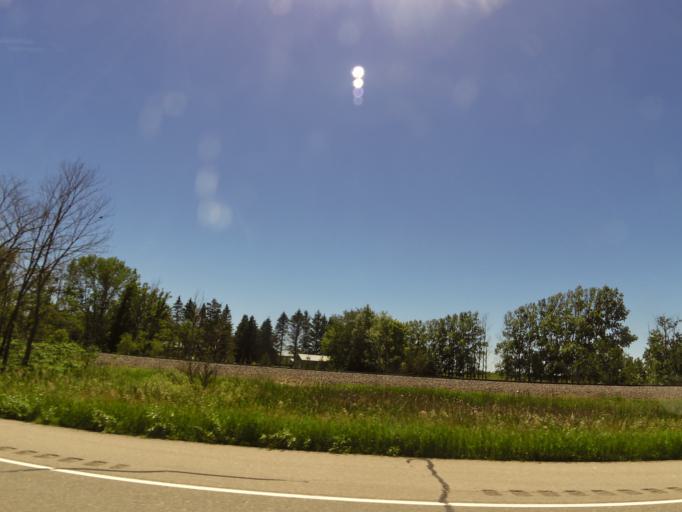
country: US
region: Minnesota
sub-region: Otter Tail County
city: New York Mills
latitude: 46.5383
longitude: -95.4331
